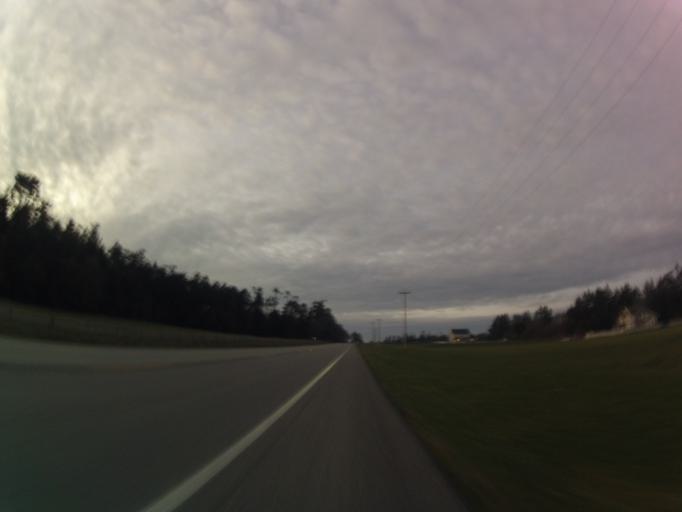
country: US
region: Washington
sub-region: Island County
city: Coupeville
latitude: 48.1732
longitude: -122.6812
